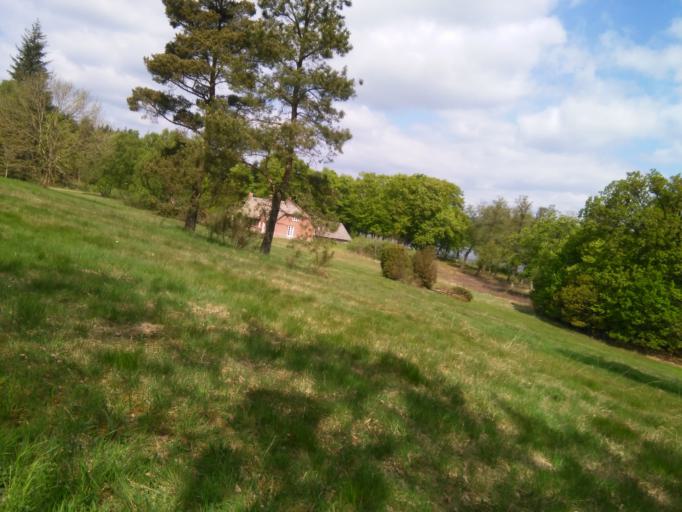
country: DK
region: Central Jutland
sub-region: Silkeborg Kommune
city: Svejbaek
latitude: 56.0618
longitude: 9.6348
